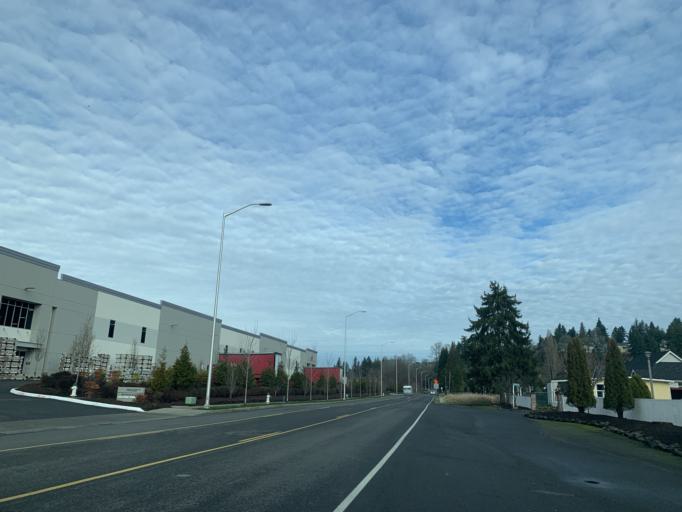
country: US
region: Washington
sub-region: Pierce County
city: Milton
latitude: 47.2230
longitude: -122.3205
